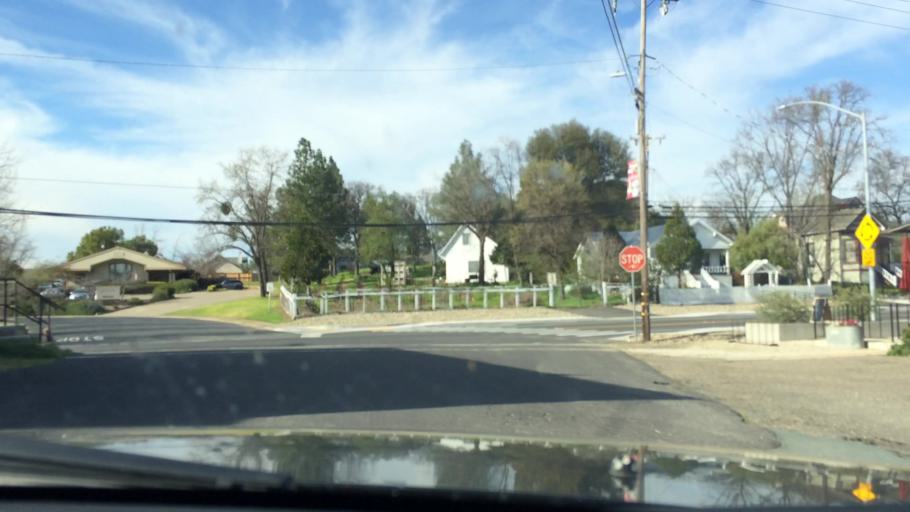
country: US
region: California
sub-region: Amador County
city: Plymouth
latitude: 38.4812
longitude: -120.8463
